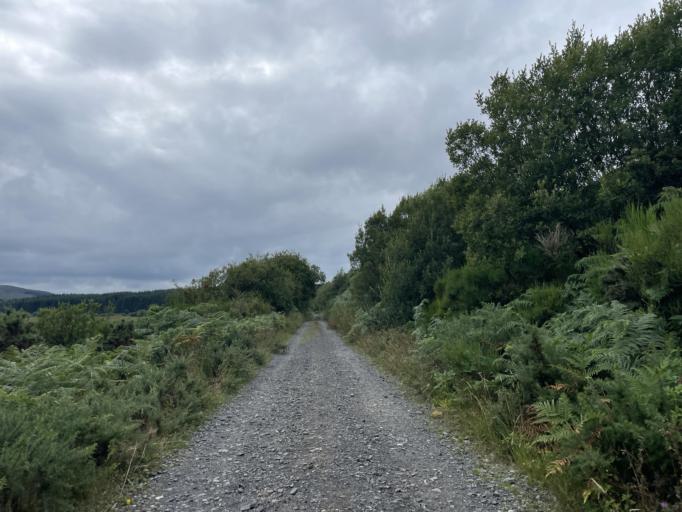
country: GB
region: Scotland
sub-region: Dumfries and Galloway
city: Newton Stewart
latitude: 54.9507
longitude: -4.2583
